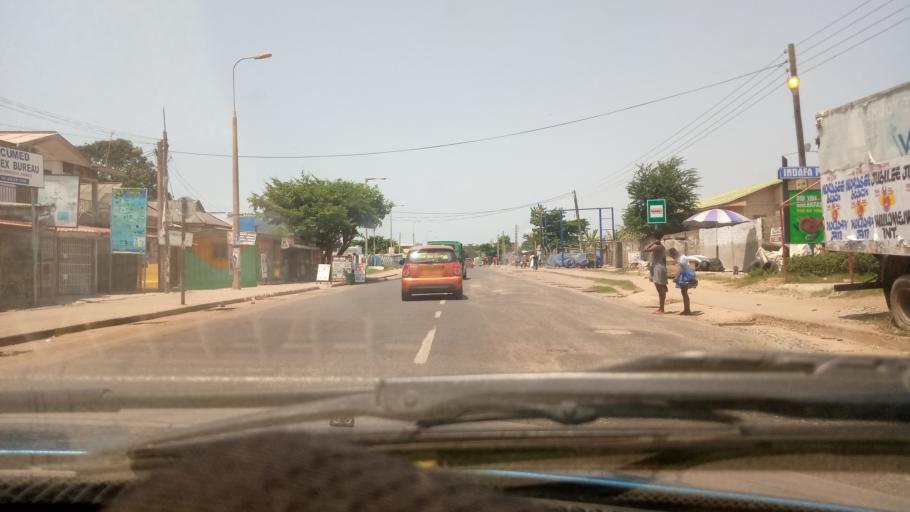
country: GH
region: Greater Accra
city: Accra
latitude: 5.5344
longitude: -0.2346
